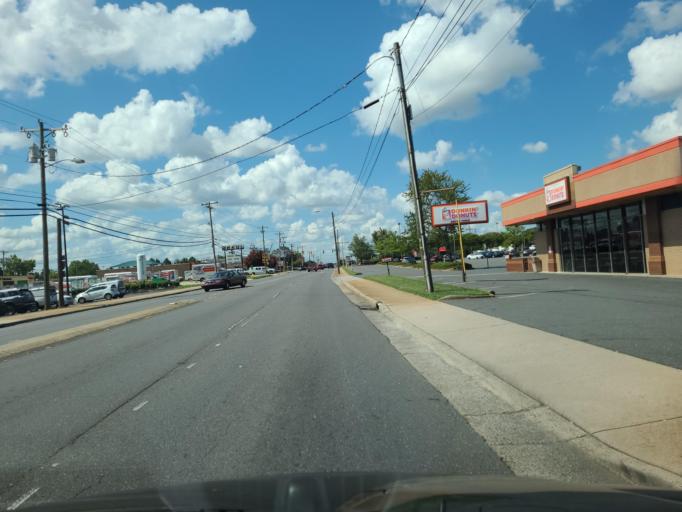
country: US
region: North Carolina
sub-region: Mecklenburg County
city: Charlotte
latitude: 35.1662
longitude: -80.8760
